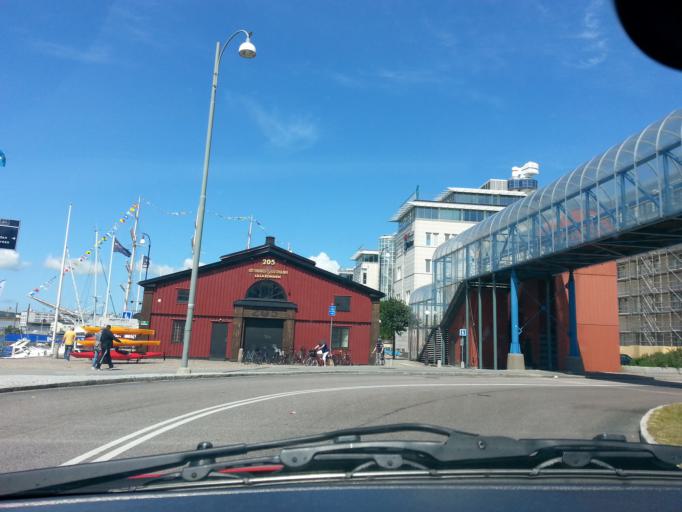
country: SE
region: Vaestra Goetaland
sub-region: Goteborg
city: Goeteborg
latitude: 57.7109
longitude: 11.9667
